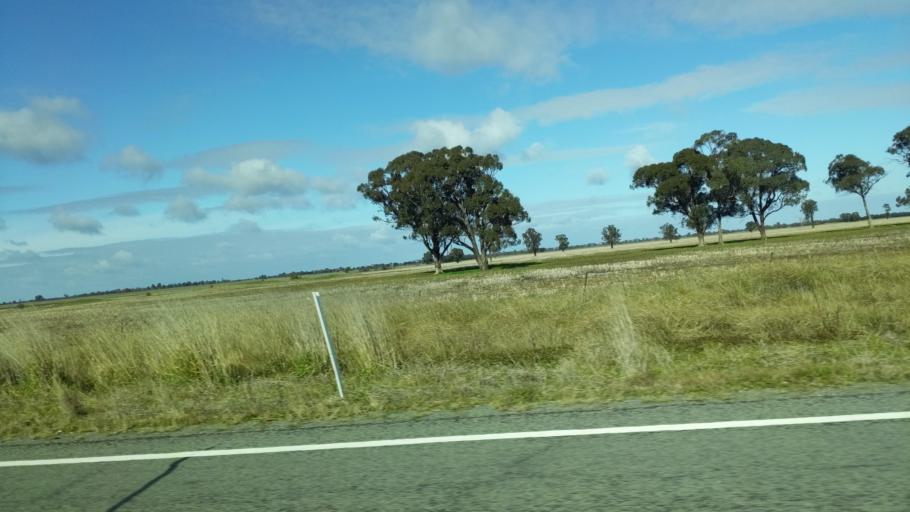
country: AU
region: New South Wales
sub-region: Narrandera
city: Narrandera
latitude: -34.7578
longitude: 146.8715
